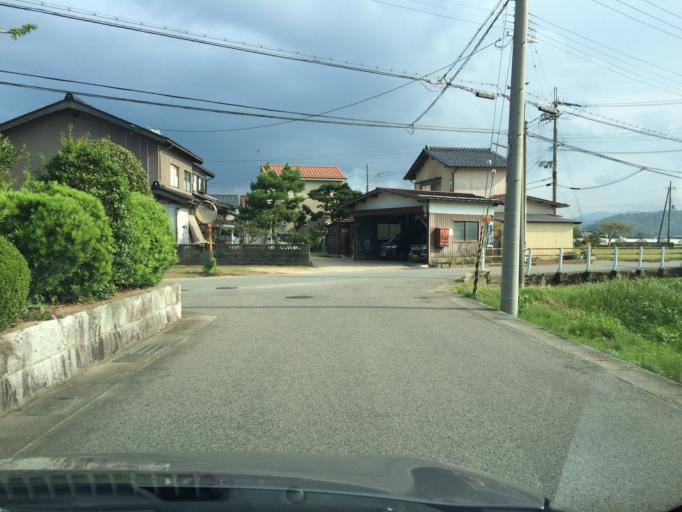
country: JP
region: Hyogo
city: Toyooka
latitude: 35.5230
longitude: 134.8274
